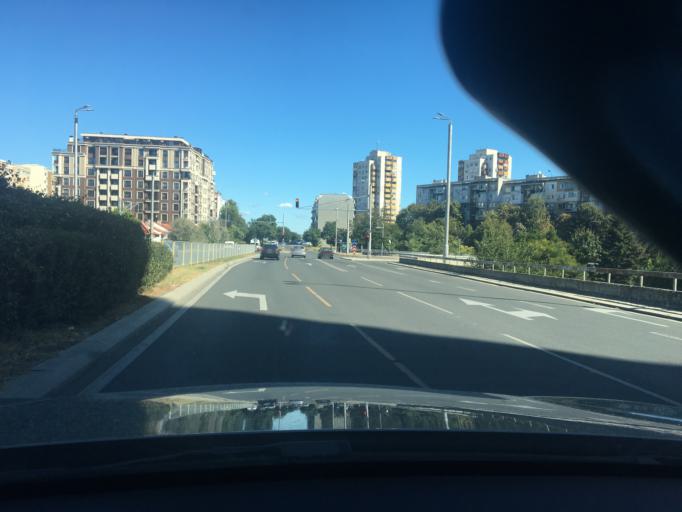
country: BG
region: Burgas
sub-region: Obshtina Burgas
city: Burgas
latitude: 42.5205
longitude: 27.4647
